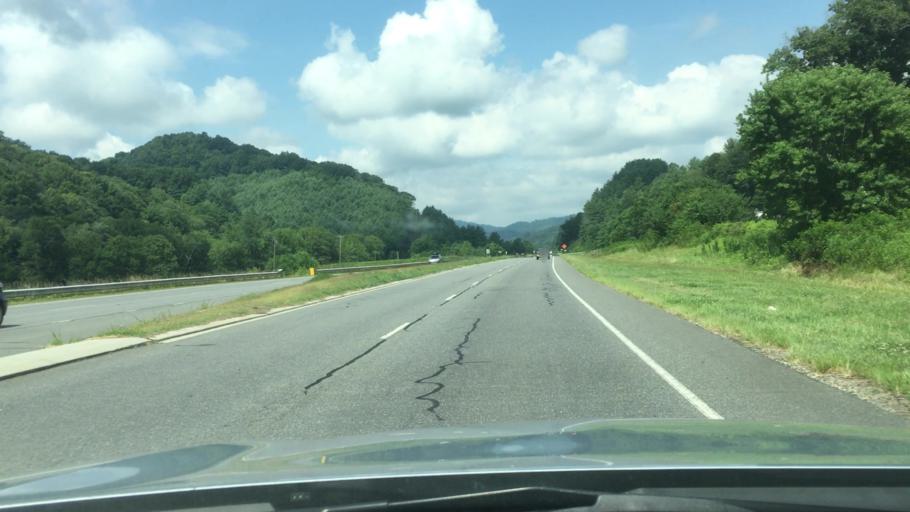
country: US
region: North Carolina
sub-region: Yancey County
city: Burnsville
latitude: 35.9135
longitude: -82.4062
